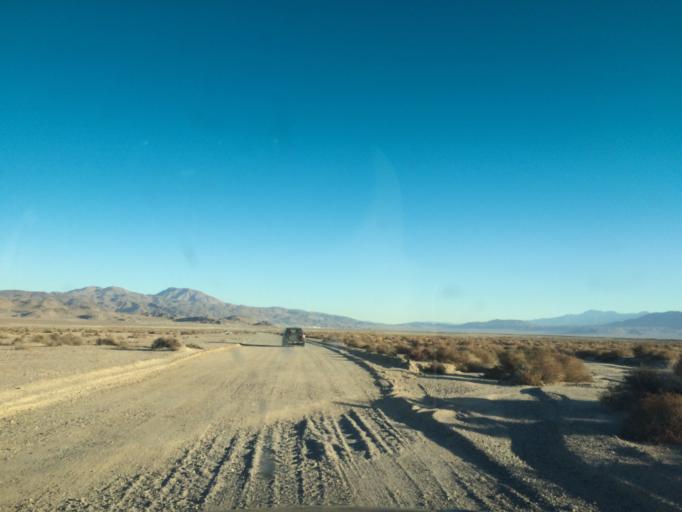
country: US
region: California
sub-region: San Bernardino County
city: Searles Valley
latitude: 35.6444
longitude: -117.3763
